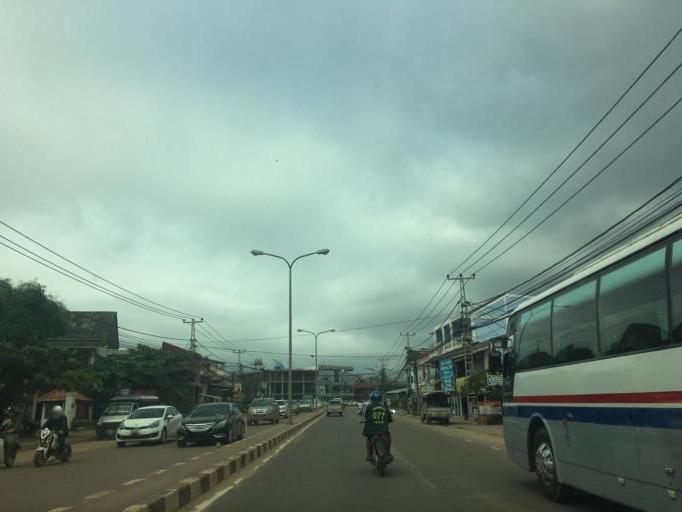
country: TH
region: Nong Khai
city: Si Chiang Mai
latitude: 17.9744
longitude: 102.5590
